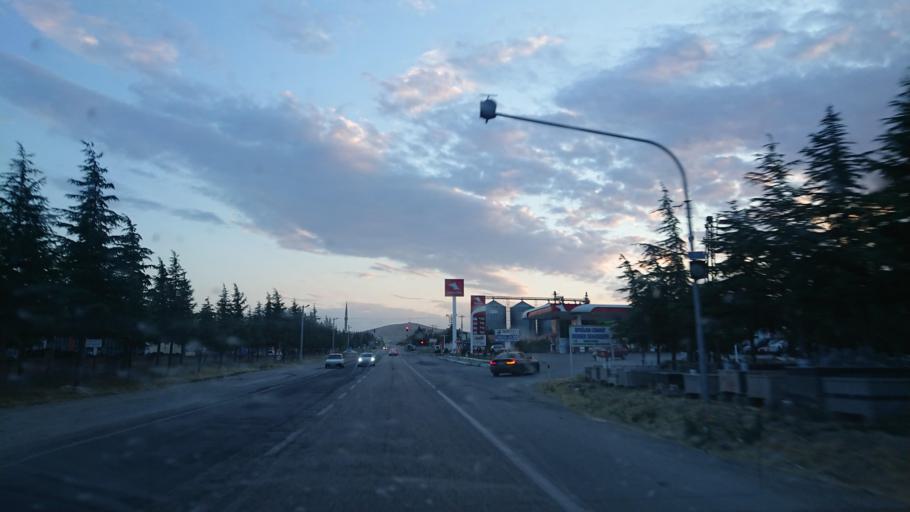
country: TR
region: Aksaray
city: Ortakoy
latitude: 38.7551
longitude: 34.0726
